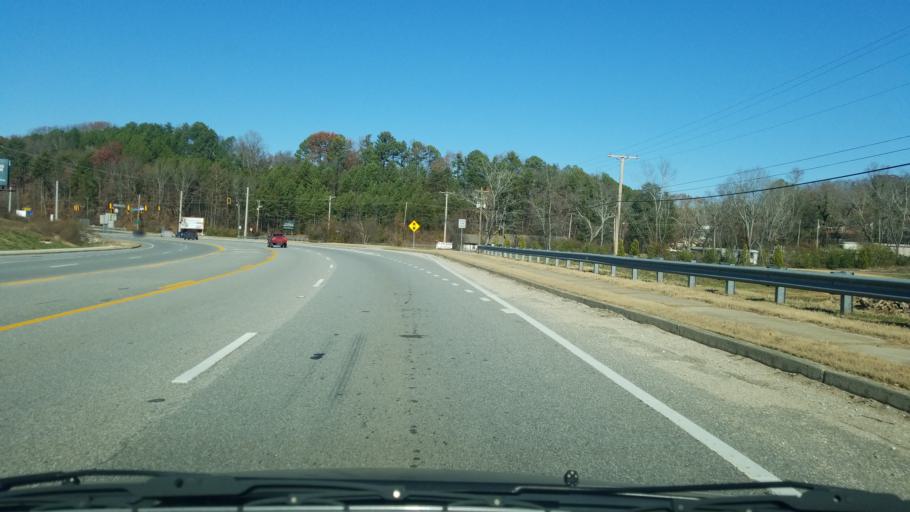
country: US
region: Georgia
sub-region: Catoosa County
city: Indian Springs
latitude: 34.9842
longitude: -85.1872
